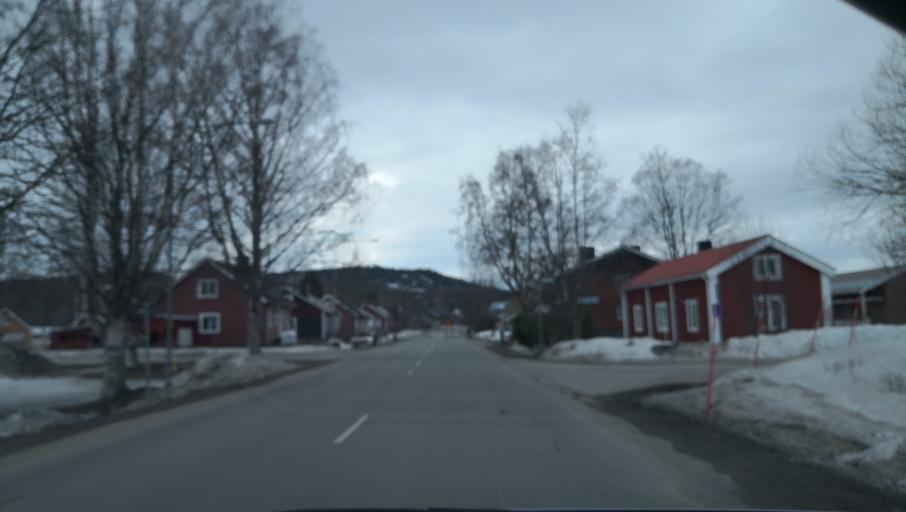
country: SE
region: Vaesterbotten
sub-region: Vannas Kommun
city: Vannasby
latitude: 63.9135
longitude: 19.8310
